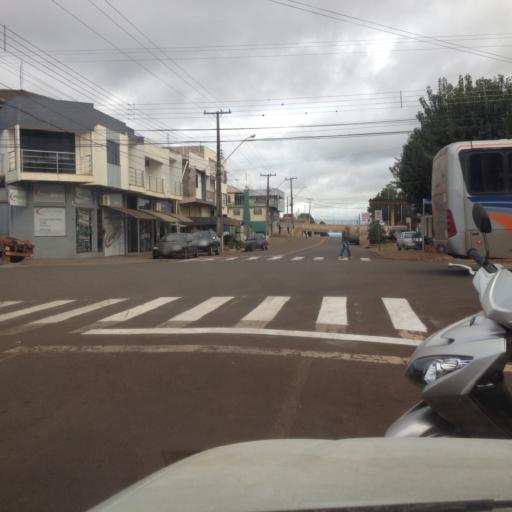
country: BR
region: Parana
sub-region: Matelandia
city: Matelandia
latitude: -25.2414
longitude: -53.9757
